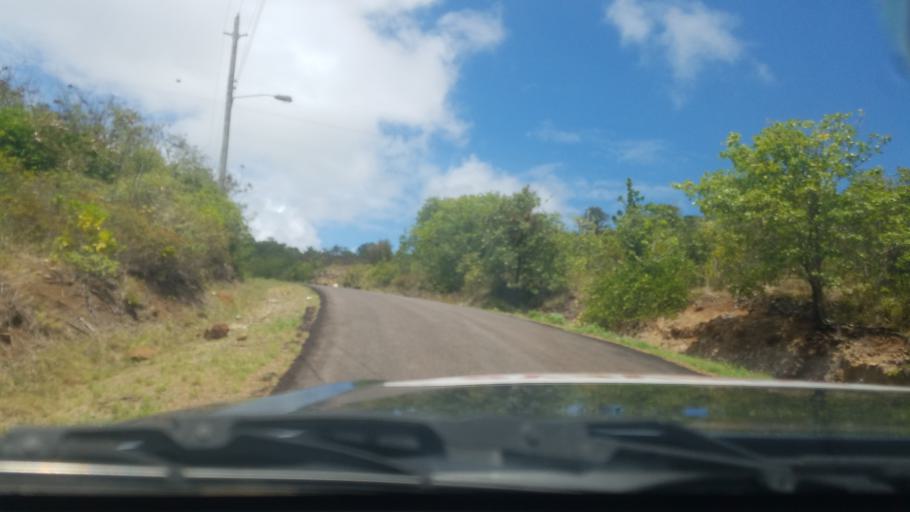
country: LC
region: Dennery Quarter
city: Dennery
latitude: 13.8993
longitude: -60.8916
